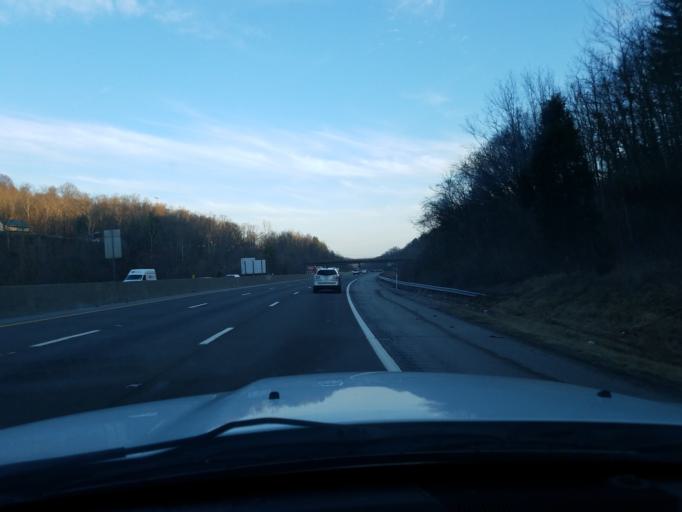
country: US
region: West Virginia
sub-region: Kanawha County
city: Nitro
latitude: 38.4313
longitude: -81.8259
